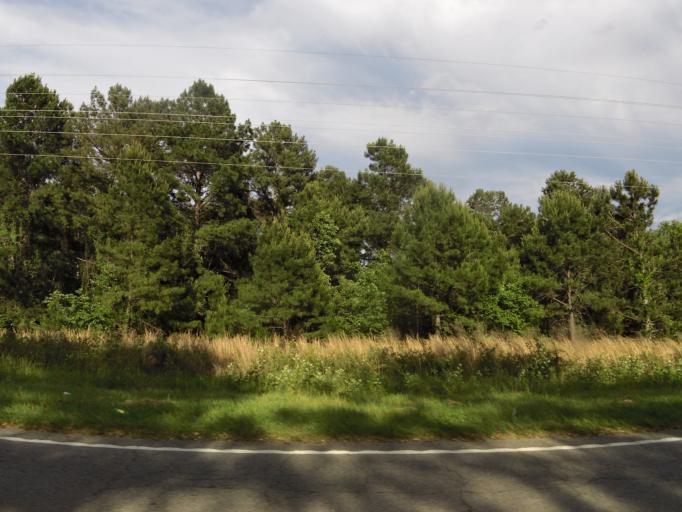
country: US
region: South Carolina
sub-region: Hampton County
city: Estill
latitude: 32.7813
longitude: -81.2407
